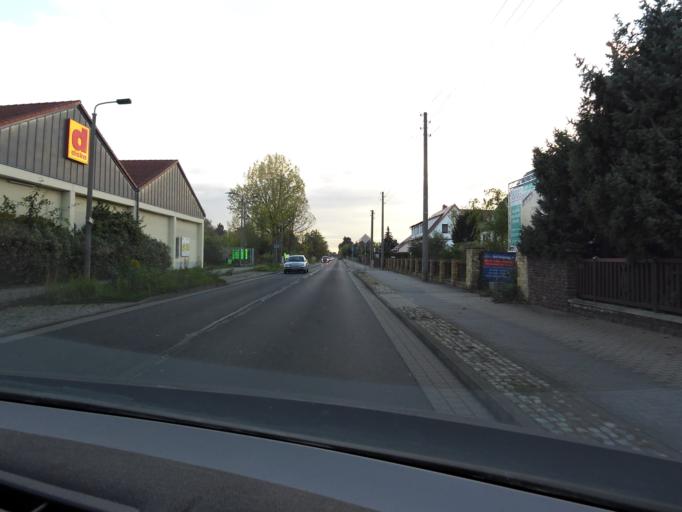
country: DE
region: Saxony
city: Leipzig
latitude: 51.3904
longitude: 12.3274
